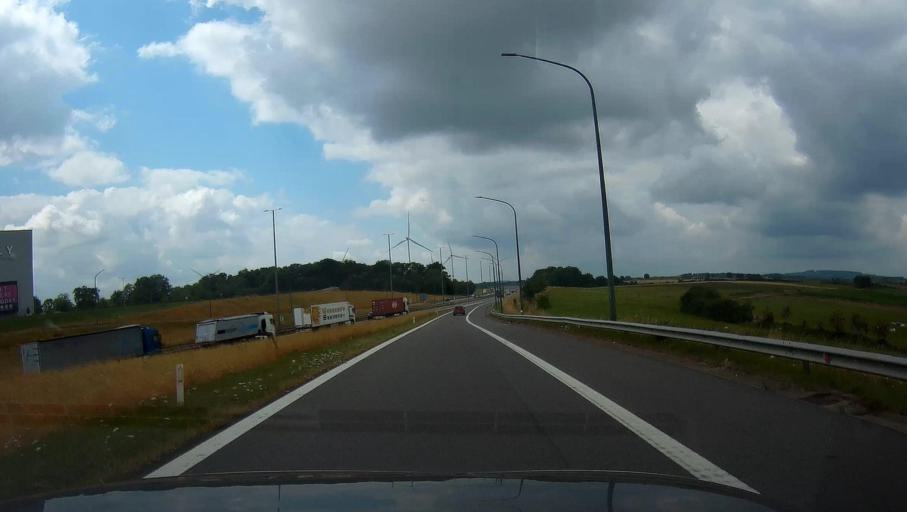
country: LU
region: Luxembourg
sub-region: Canton de Capellen
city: Steinfort
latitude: 49.6408
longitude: 5.8863
